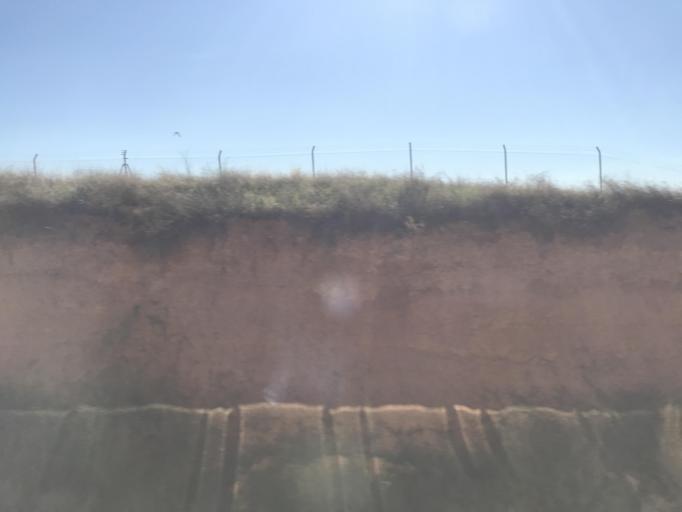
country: ES
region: Castille-La Mancha
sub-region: Provincia de Guadalajara
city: Almadrones
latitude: 40.8734
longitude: -2.7636
